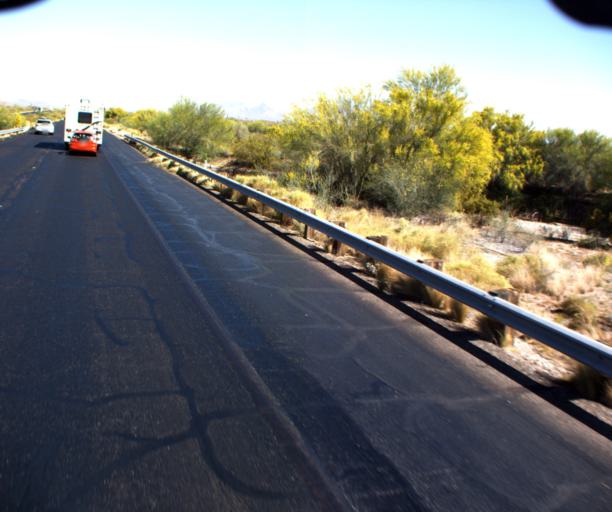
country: US
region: Arizona
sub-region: Pinal County
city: Maricopa
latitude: 32.8477
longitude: -112.3043
